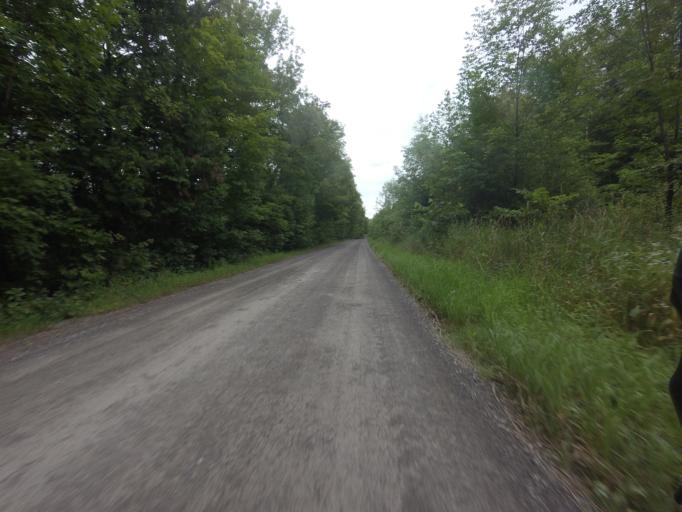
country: CA
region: Ontario
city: Carleton Place
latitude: 45.1469
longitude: -76.2239
